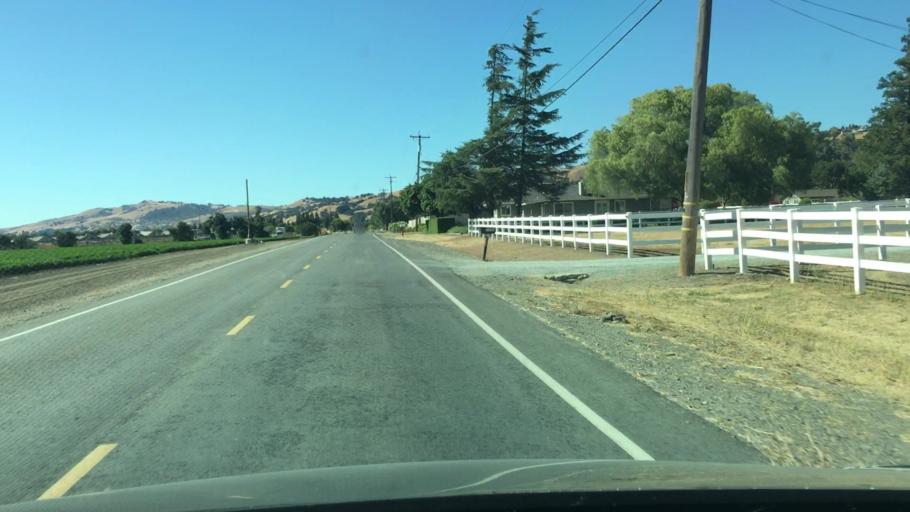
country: US
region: California
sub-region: Santa Clara County
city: San Martin
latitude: 37.1229
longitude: -121.5971
